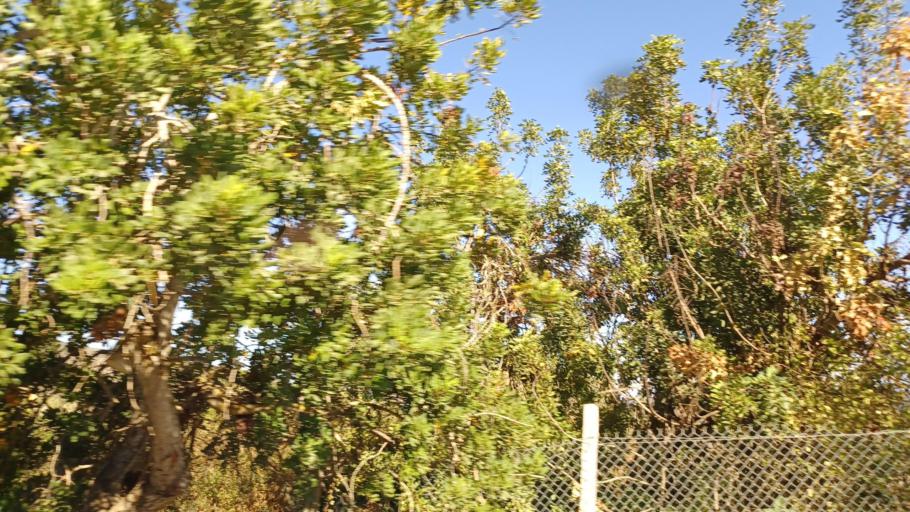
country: CY
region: Pafos
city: Polis
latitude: 35.0240
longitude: 32.3422
